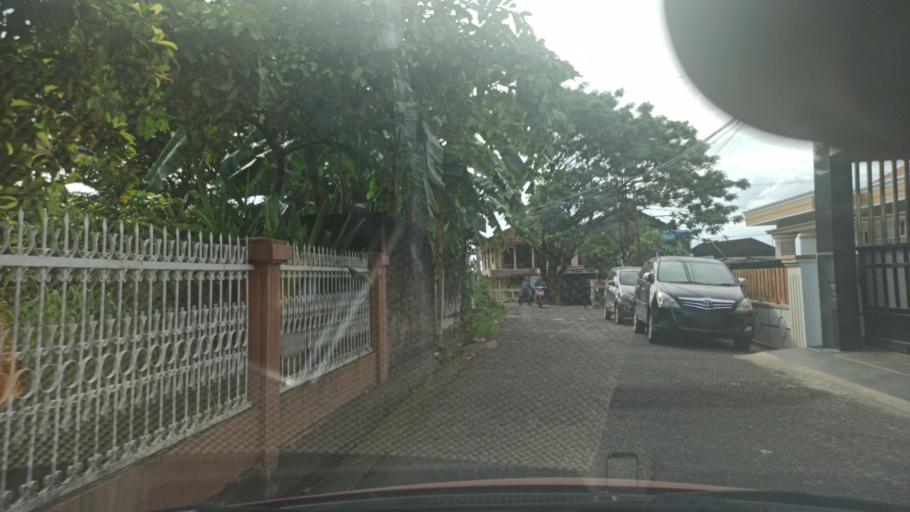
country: ID
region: South Sumatra
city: Plaju
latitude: -2.9923
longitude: 104.7241
